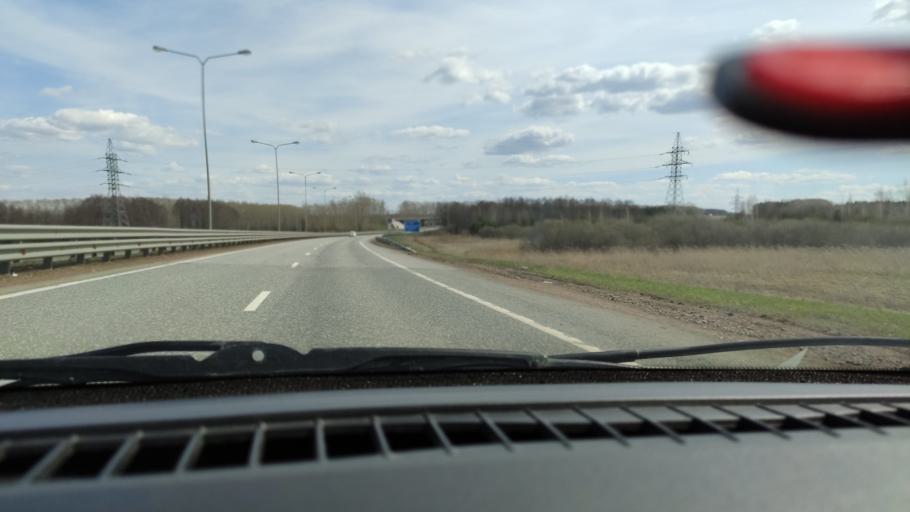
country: RU
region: Bashkortostan
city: Kushnarenkovo
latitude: 55.0582
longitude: 55.4275
